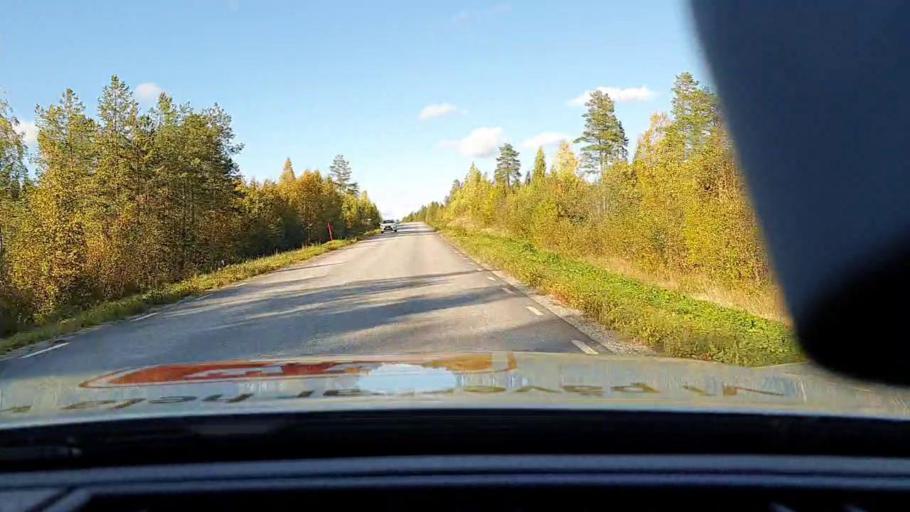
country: SE
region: Norrbotten
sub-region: Pitea Kommun
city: Norrfjarden
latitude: 65.4930
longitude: 21.4736
